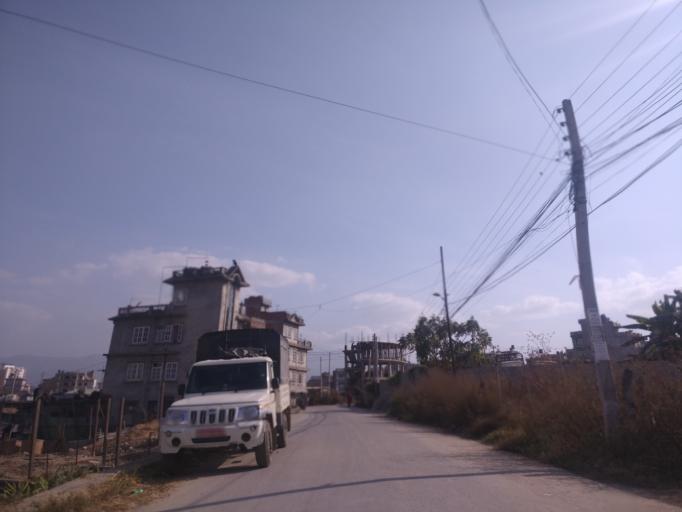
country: NP
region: Central Region
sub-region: Bagmati Zone
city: Patan
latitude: 27.6765
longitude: 85.3324
